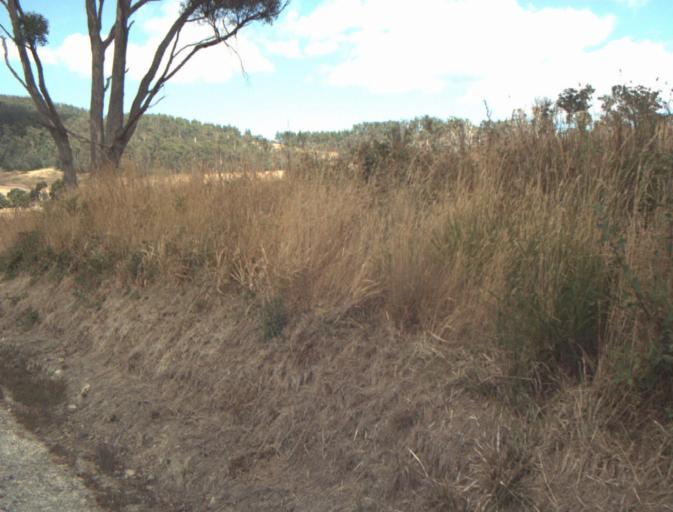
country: AU
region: Tasmania
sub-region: Launceston
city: Mayfield
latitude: -41.2107
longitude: 147.1091
